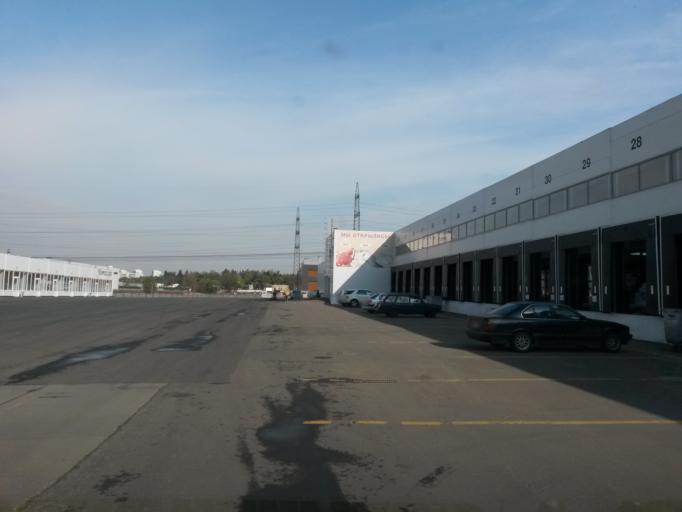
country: RU
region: Moskovskaya
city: Mosrentgen
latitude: 55.5993
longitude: 37.4629
